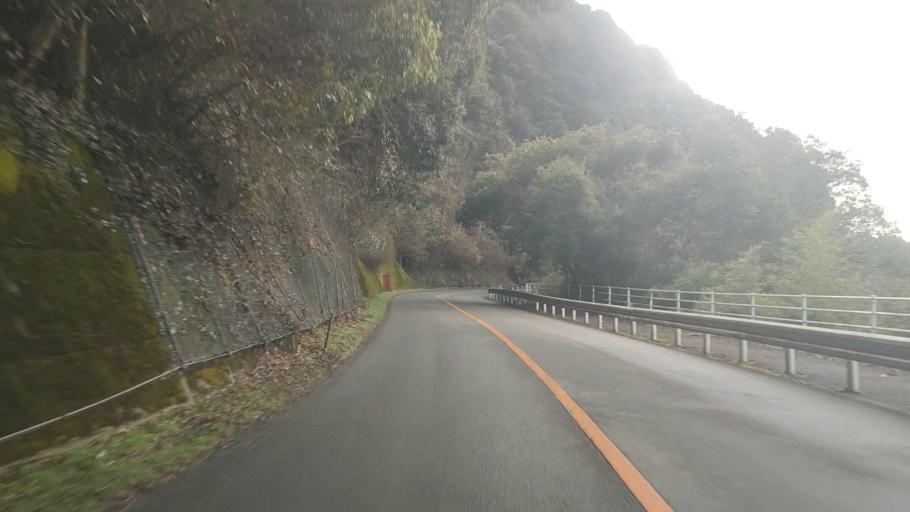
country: JP
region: Kumamoto
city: Hitoyoshi
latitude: 32.3006
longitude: 130.8464
